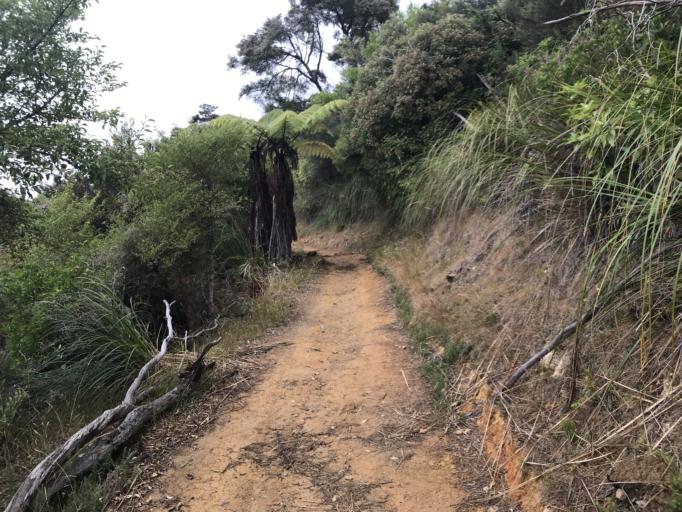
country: NZ
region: Marlborough
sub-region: Marlborough District
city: Picton
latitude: -41.2274
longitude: 173.9592
